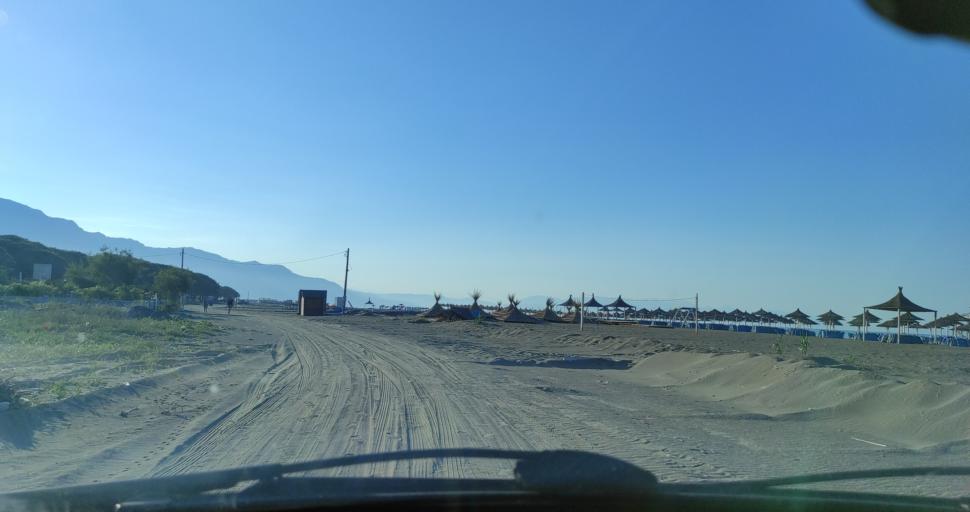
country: AL
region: Shkoder
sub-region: Rrethi i Shkodres
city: Velipoje
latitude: 41.8604
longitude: 19.4361
